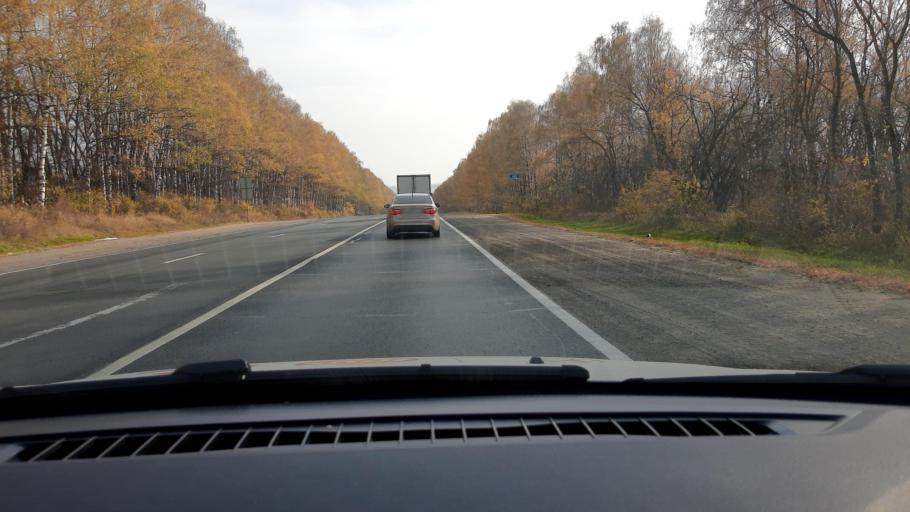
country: RU
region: Nizjnij Novgorod
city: Pamyat' Parizhskoy Kommuny
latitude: 56.0541
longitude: 44.4042
